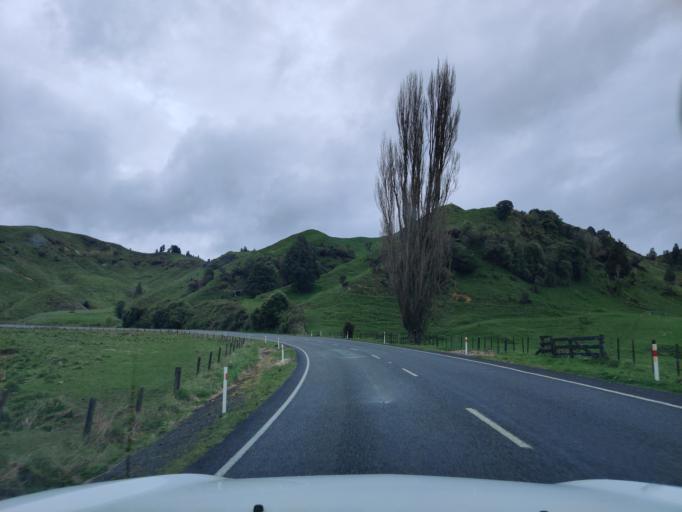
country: NZ
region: Waikato
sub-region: Otorohanga District
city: Otorohanga
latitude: -38.5532
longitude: 175.1960
